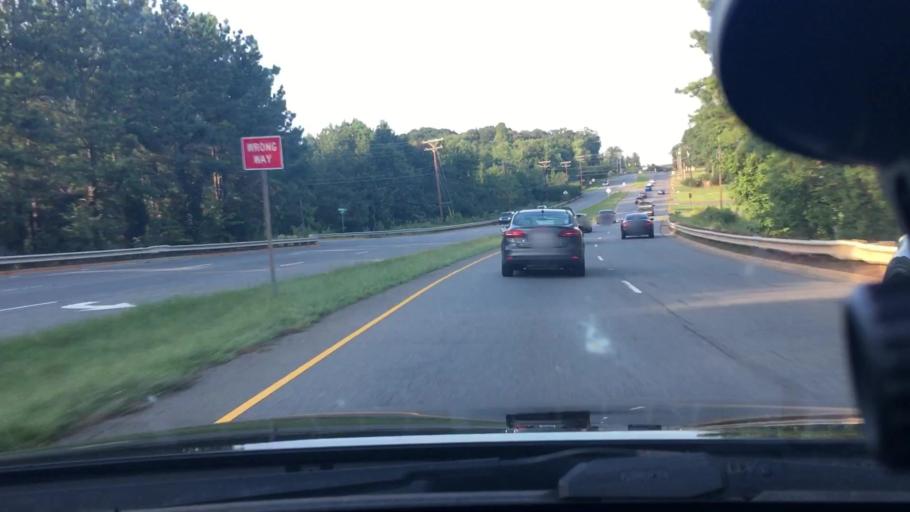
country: US
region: North Carolina
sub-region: Mecklenburg County
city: Mint Hill
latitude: 35.2130
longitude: -80.6611
